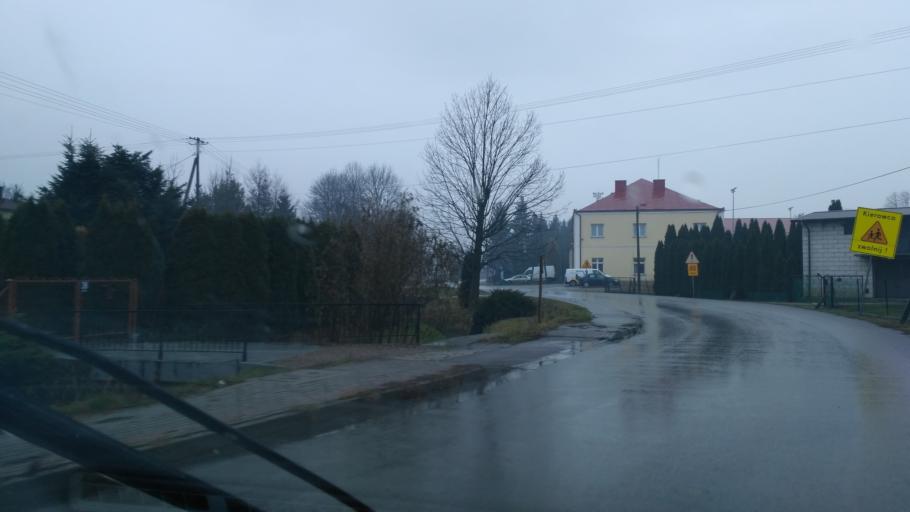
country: PL
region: Subcarpathian Voivodeship
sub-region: Powiat rzeszowski
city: Krasne
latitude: 50.0750
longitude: 22.1274
